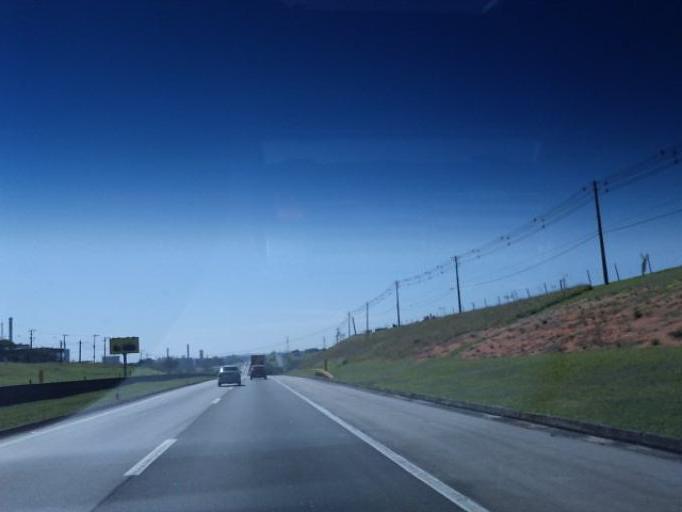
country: BR
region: Sao Paulo
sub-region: Cacapava
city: Cacapava
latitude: -23.1414
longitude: -45.7642
